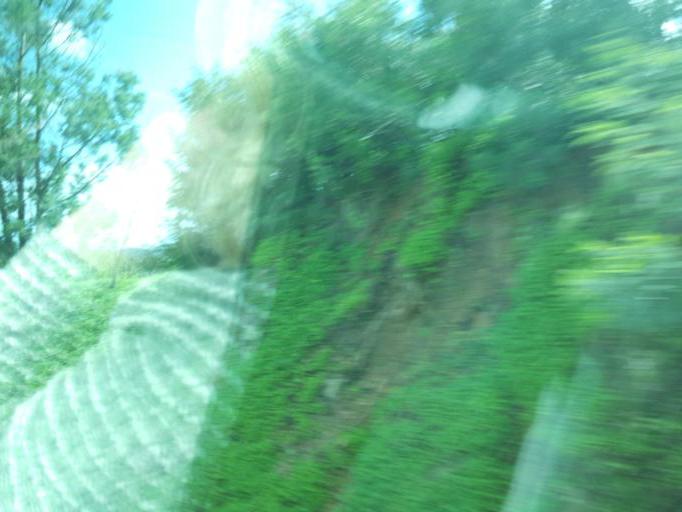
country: PT
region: Faro
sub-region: Monchique
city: Monchique
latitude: 37.2791
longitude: -8.5523
